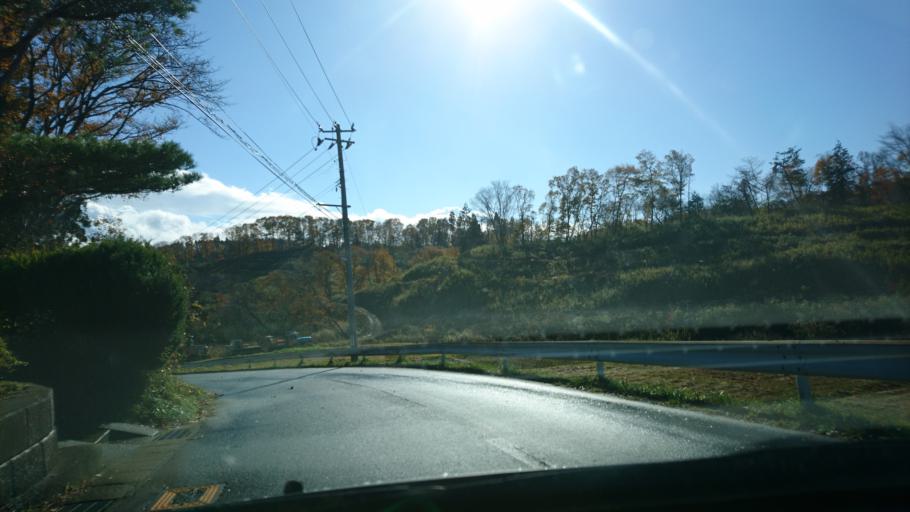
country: JP
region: Iwate
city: Ichinoseki
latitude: 38.9469
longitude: 141.1081
